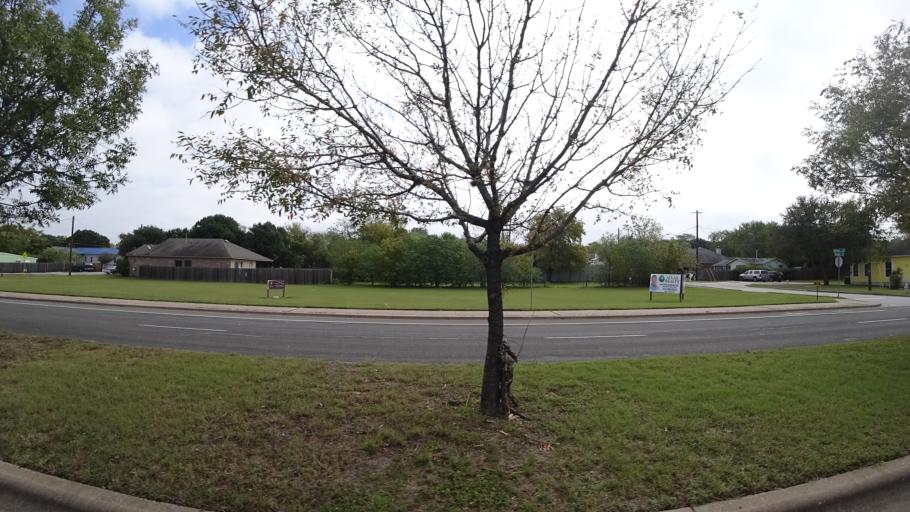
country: US
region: Texas
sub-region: Travis County
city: Shady Hollow
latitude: 30.2037
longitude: -97.8370
